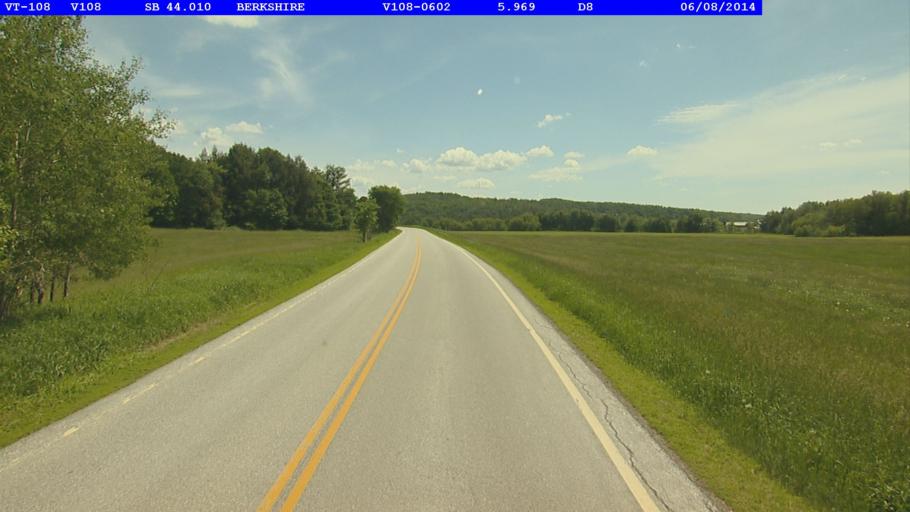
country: US
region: Vermont
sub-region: Franklin County
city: Enosburg Falls
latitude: 45.0030
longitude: -72.8255
